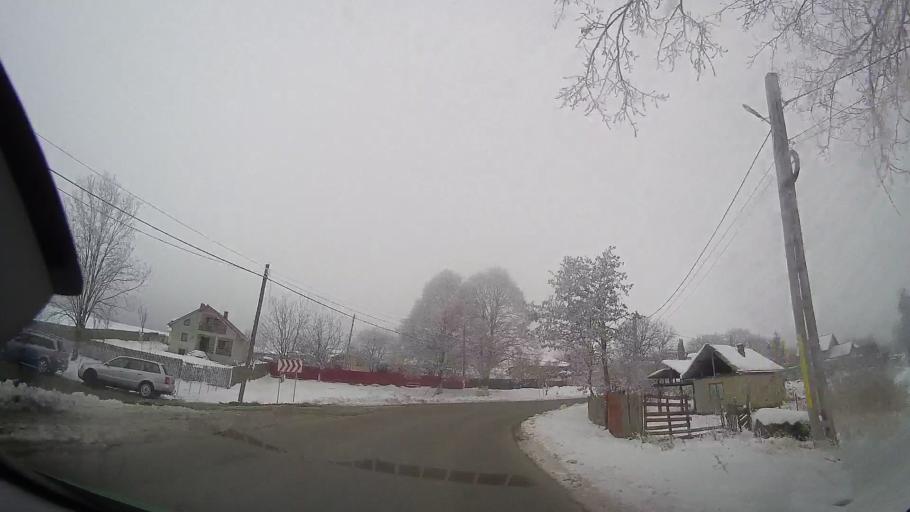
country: RO
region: Neamt
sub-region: Comuna Icusesti
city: Balusesti
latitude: 46.8605
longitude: 27.0082
